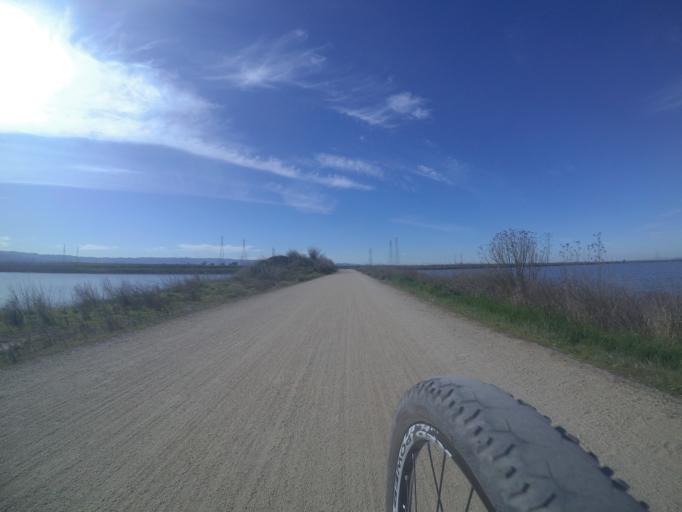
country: US
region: California
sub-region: Santa Clara County
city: Mountain View
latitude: 37.4345
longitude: -122.0655
